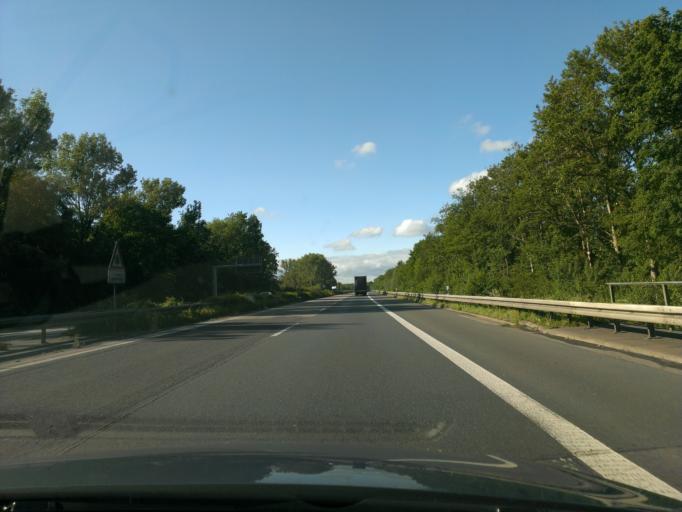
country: DE
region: North Rhine-Westphalia
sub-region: Regierungsbezirk Munster
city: Senden
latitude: 51.8751
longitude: 7.5762
